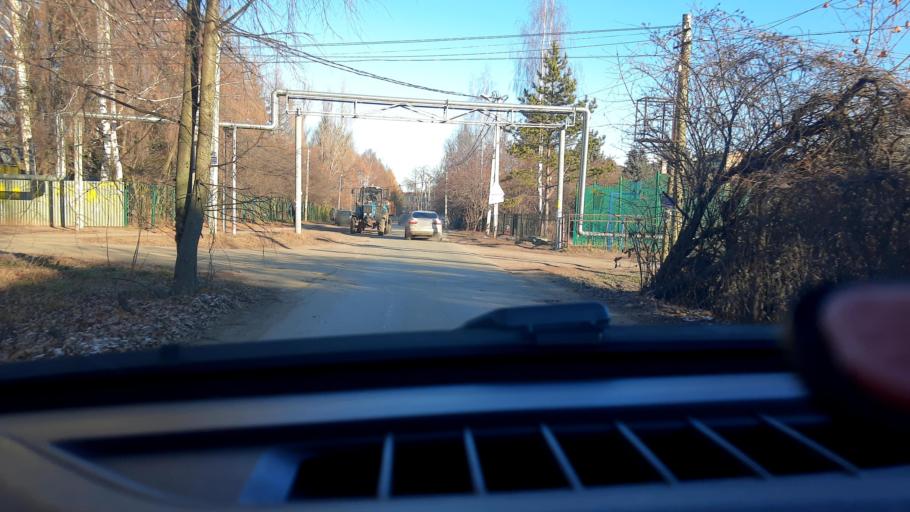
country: RU
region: Nizjnij Novgorod
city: Burevestnik
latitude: 56.2024
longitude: 43.8792
